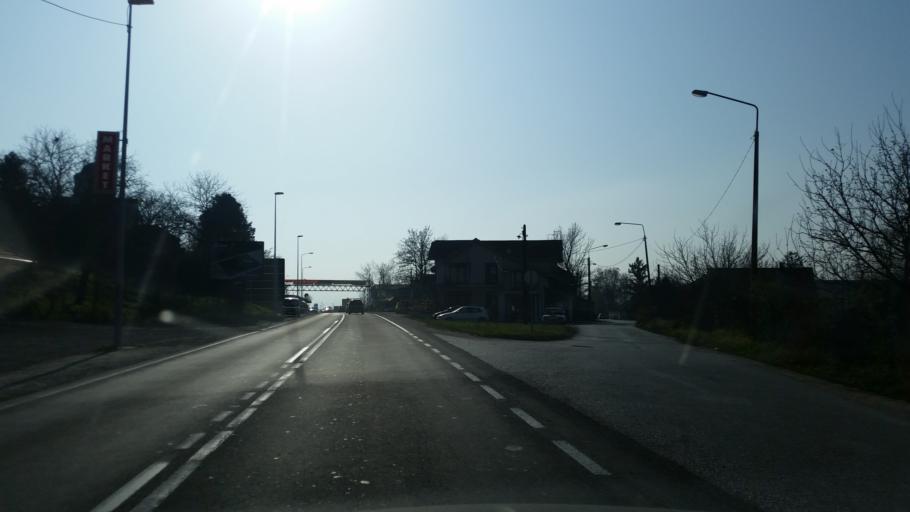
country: RS
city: Prislonica
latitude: 43.9173
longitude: 20.4078
